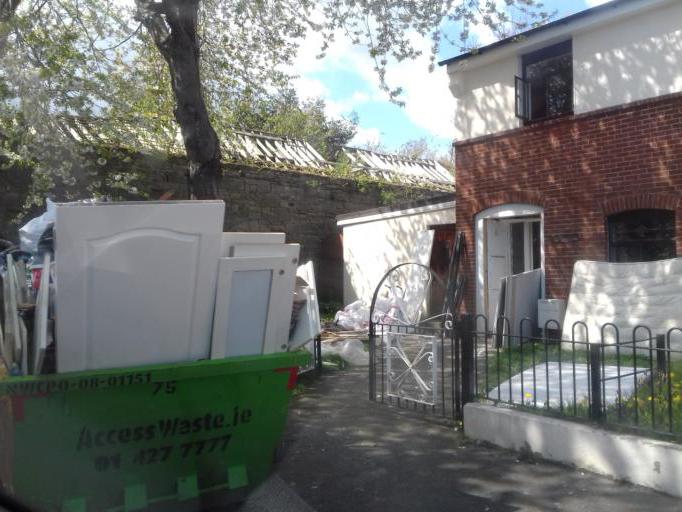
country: IE
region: Leinster
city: Rialto
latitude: 53.3501
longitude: -6.2942
